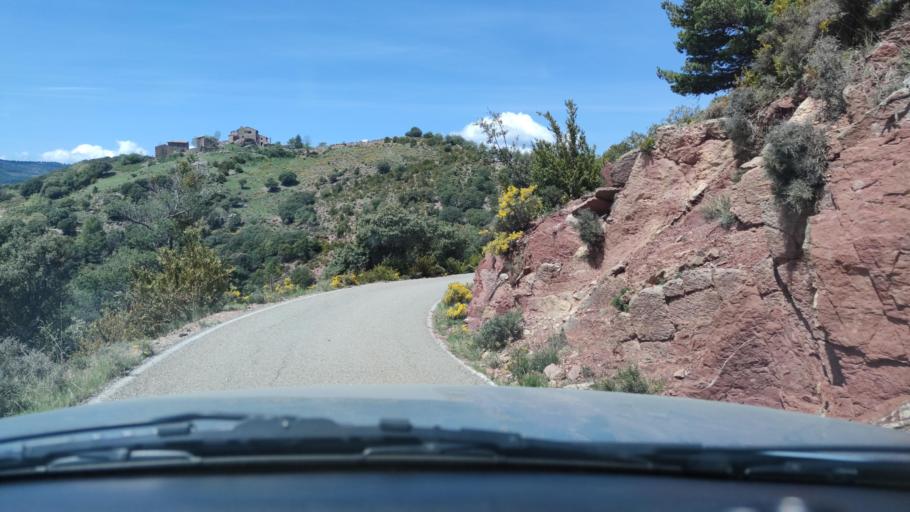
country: ES
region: Catalonia
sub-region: Provincia de Lleida
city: Sort
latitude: 42.3069
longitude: 1.1214
